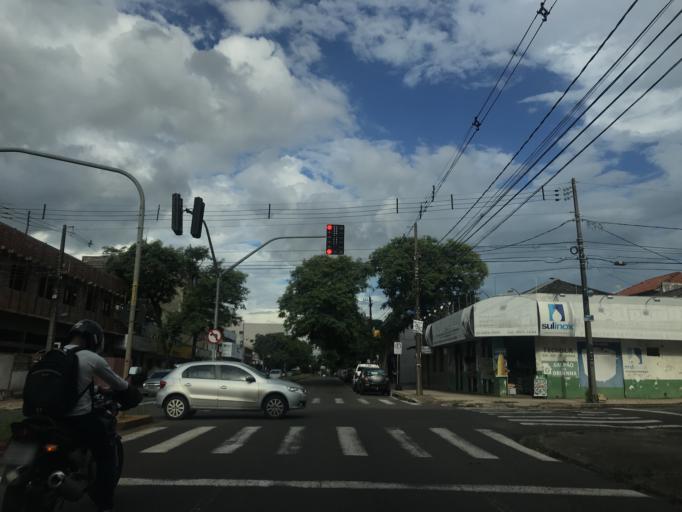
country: BR
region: Parana
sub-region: Maringa
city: Maringa
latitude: -23.4239
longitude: -51.9578
